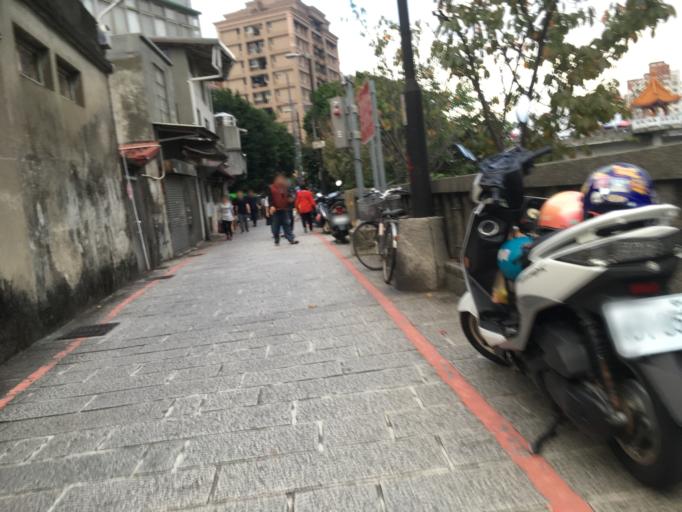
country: TW
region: Taiwan
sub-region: Taoyuan
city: Taoyuan
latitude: 24.9331
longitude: 121.3702
